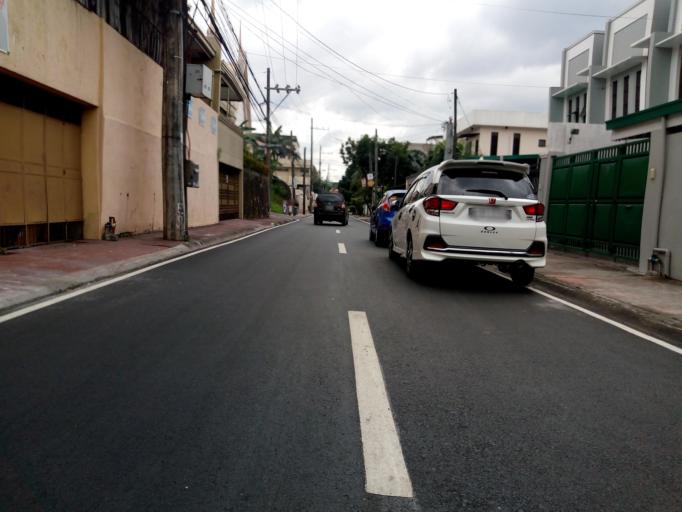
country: PH
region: Calabarzon
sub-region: Province of Rizal
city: Antipolo
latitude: 14.6399
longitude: 121.1192
